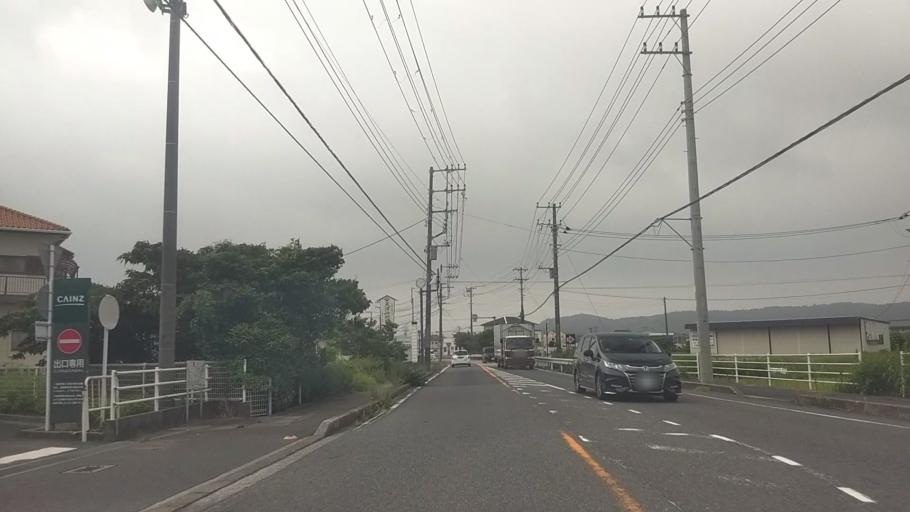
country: JP
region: Chiba
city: Kawaguchi
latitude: 35.1145
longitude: 140.0937
